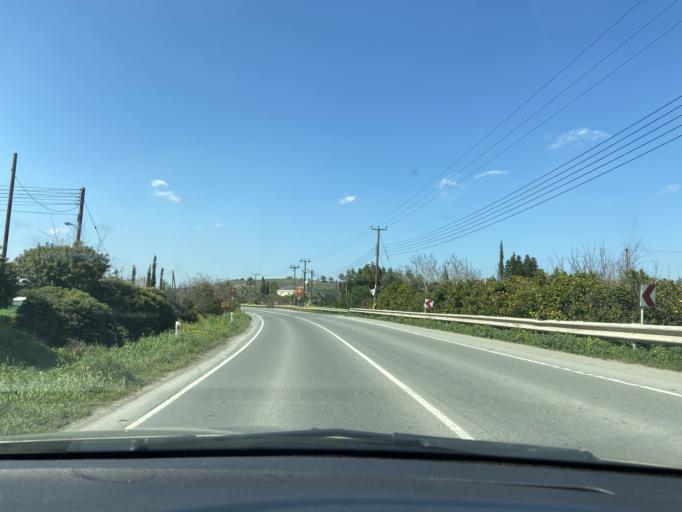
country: CY
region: Lefkosia
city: Dali
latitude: 35.0237
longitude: 33.3940
